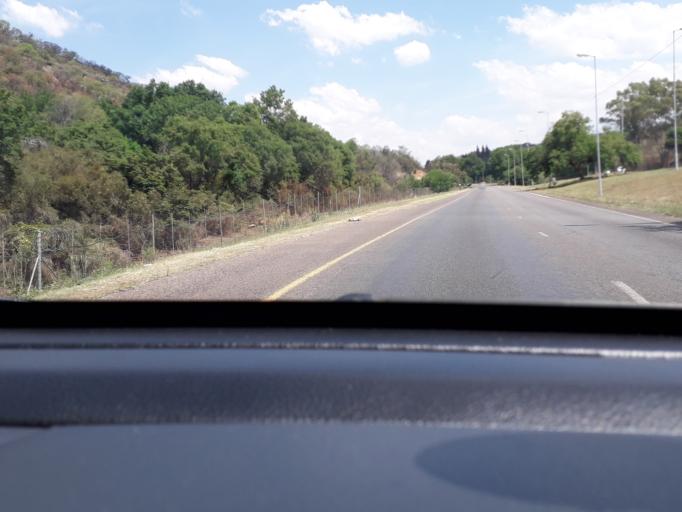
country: ZA
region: Gauteng
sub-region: City of Tshwane Metropolitan Municipality
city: Pretoria
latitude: -25.7920
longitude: 28.1965
